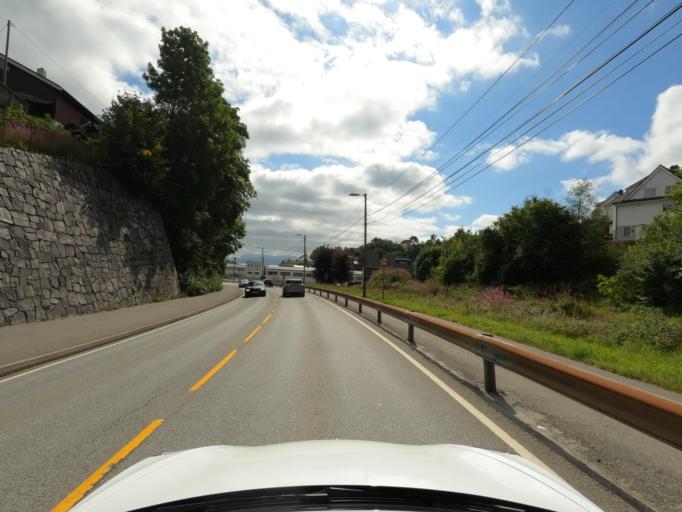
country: NO
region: Hordaland
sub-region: Os
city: Osoyro
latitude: 60.1902
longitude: 5.4637
